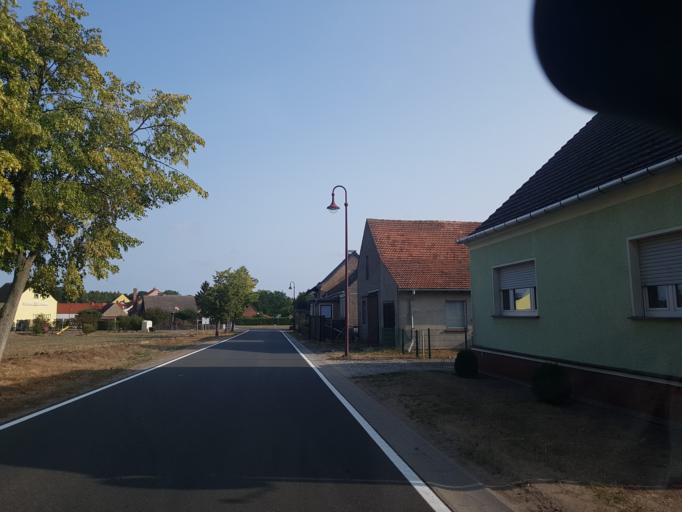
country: DE
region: Brandenburg
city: Wiesenburg
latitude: 52.0659
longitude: 12.3847
